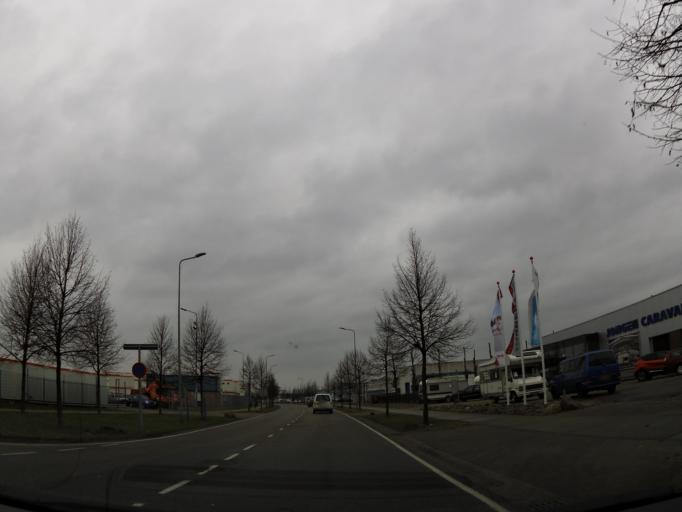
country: NL
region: Limburg
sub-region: Gemeente Sittard-Geleen
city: Sittard
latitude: 51.0129
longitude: 5.8741
